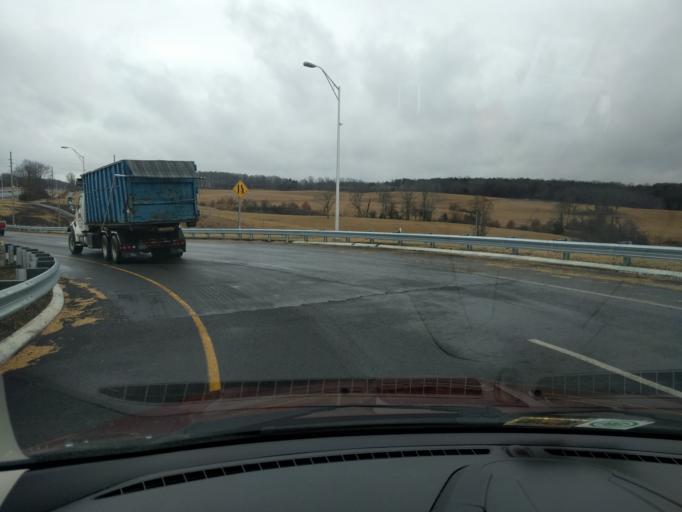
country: US
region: Virginia
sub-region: Montgomery County
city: Merrimac
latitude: 37.2089
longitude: -80.4277
